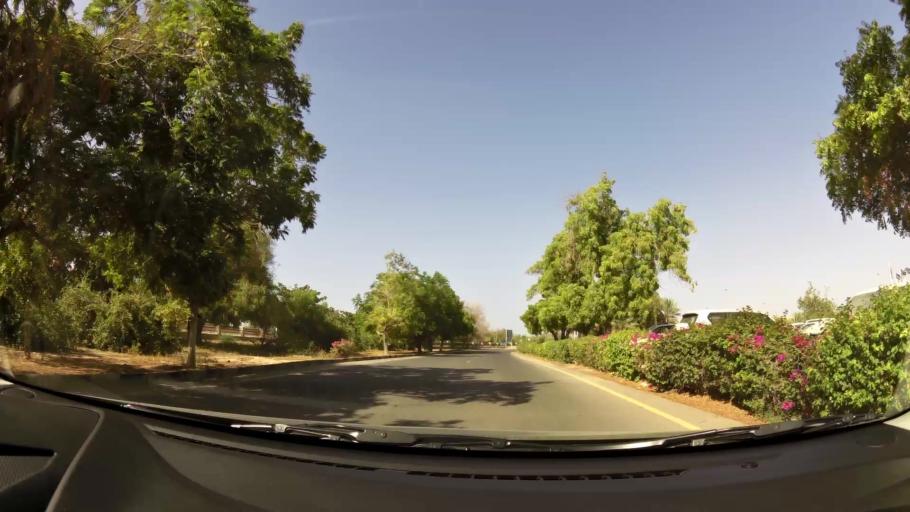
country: OM
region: Muhafazat Masqat
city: Bawshar
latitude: 23.5860
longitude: 58.3032
